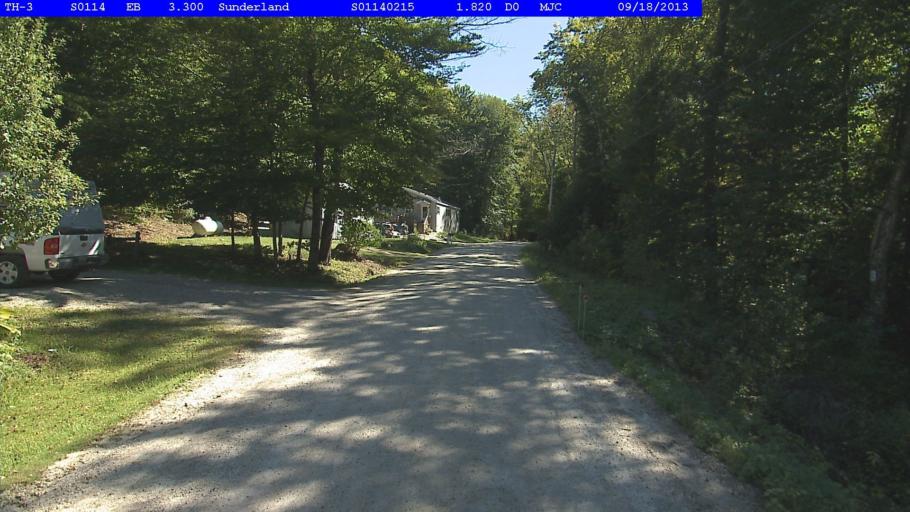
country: US
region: Vermont
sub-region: Bennington County
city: Arlington
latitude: 43.0474
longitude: -73.1165
